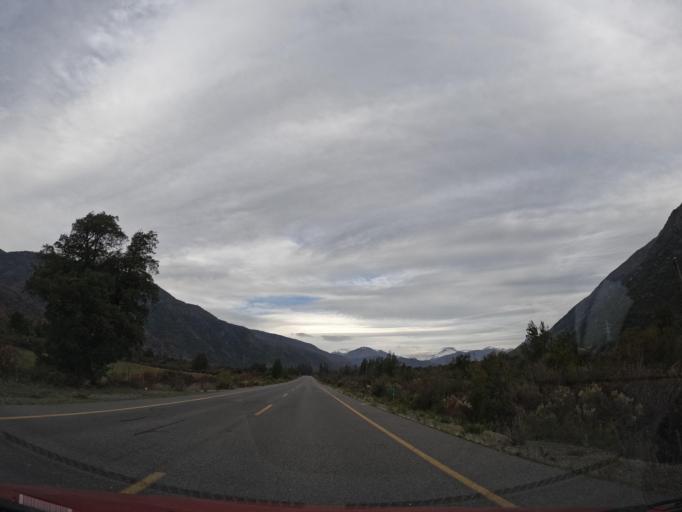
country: CL
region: Maule
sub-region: Provincia de Linares
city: Colbun
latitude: -35.7219
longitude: -71.0292
